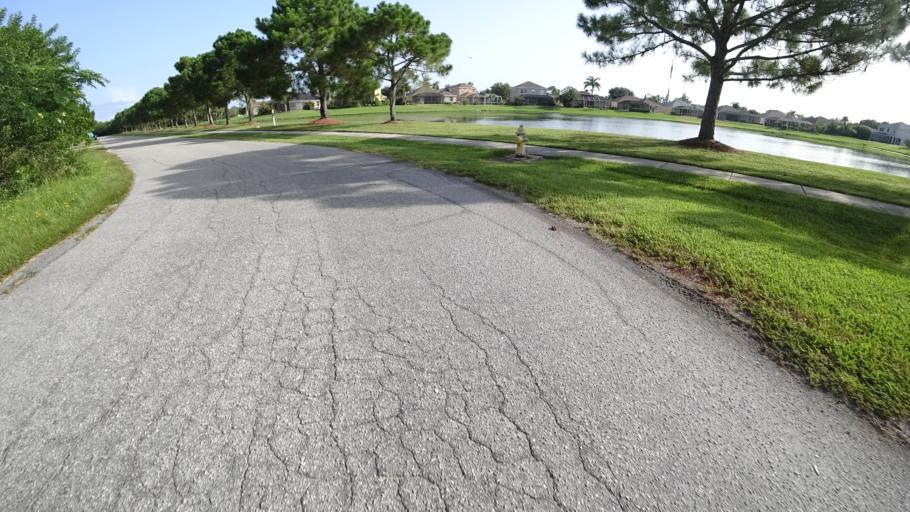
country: US
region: Florida
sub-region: Sarasota County
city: Desoto Lakes
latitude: 27.4265
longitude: -82.4766
